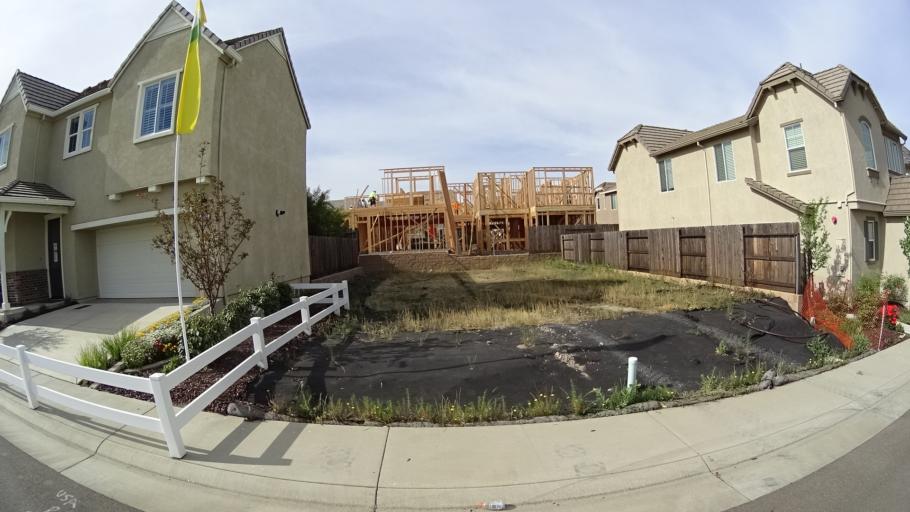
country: US
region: California
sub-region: Placer County
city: Rocklin
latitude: 38.8264
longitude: -121.2878
